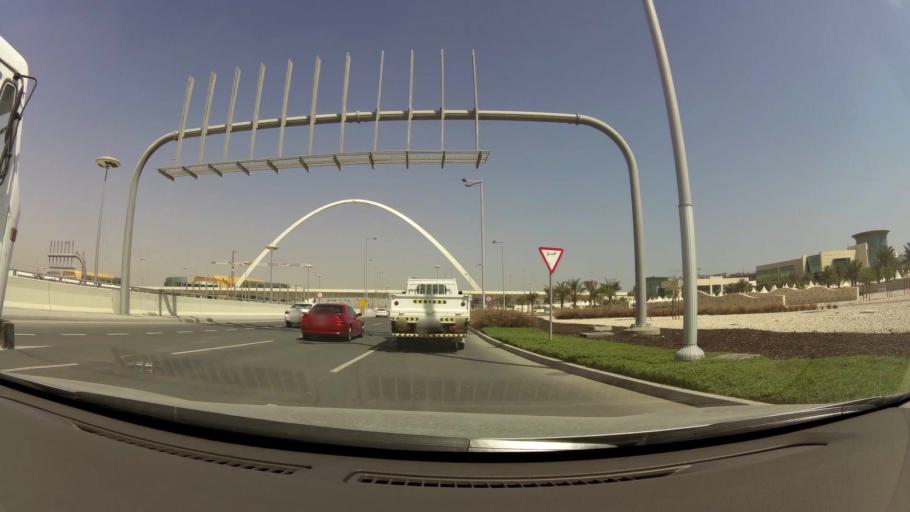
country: QA
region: Baladiyat Umm Salal
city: Umm Salal Muhammad
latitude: 25.3982
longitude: 51.5159
